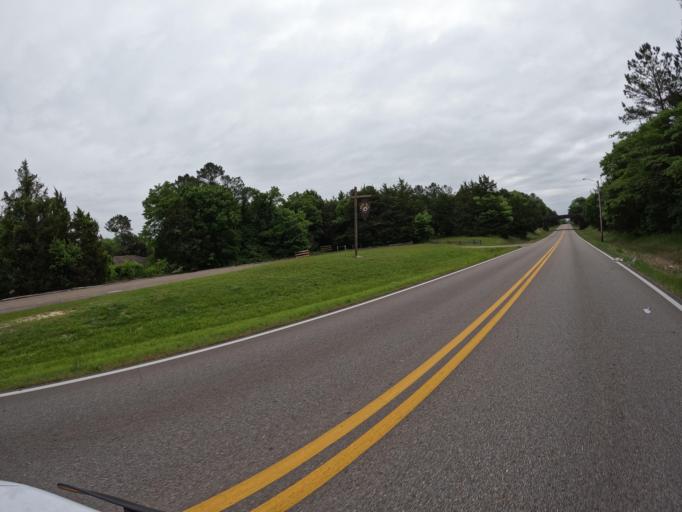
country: US
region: Mississippi
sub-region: Lee County
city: Tupelo
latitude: 34.2647
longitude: -88.7539
